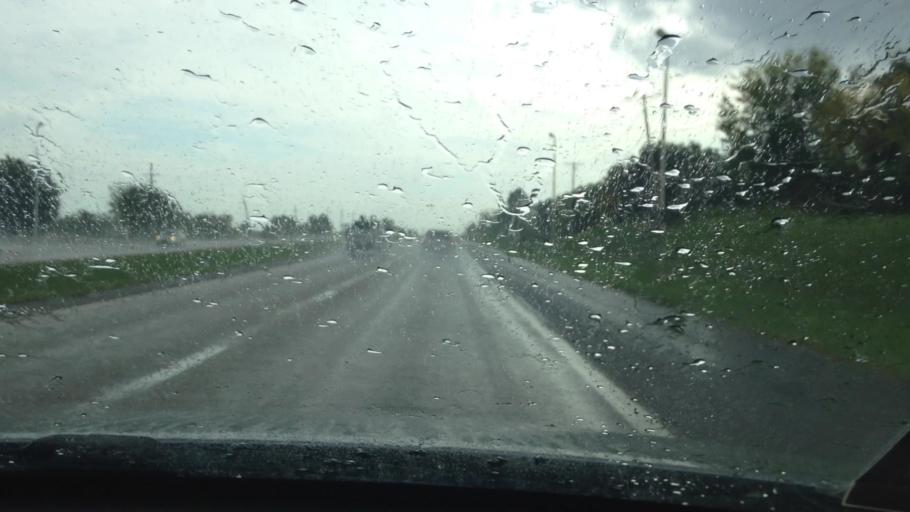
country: US
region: Kansas
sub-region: Leavenworth County
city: Basehor
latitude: 39.1856
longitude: -94.9006
